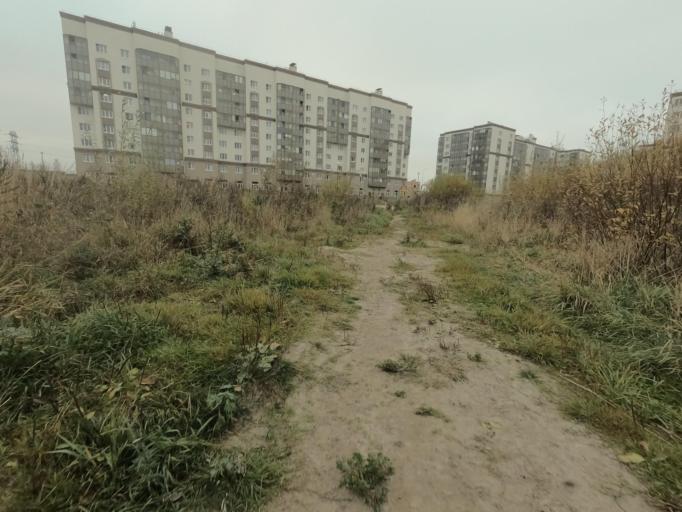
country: RU
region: Leningrad
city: Kirovsk
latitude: 59.8771
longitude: 31.0070
